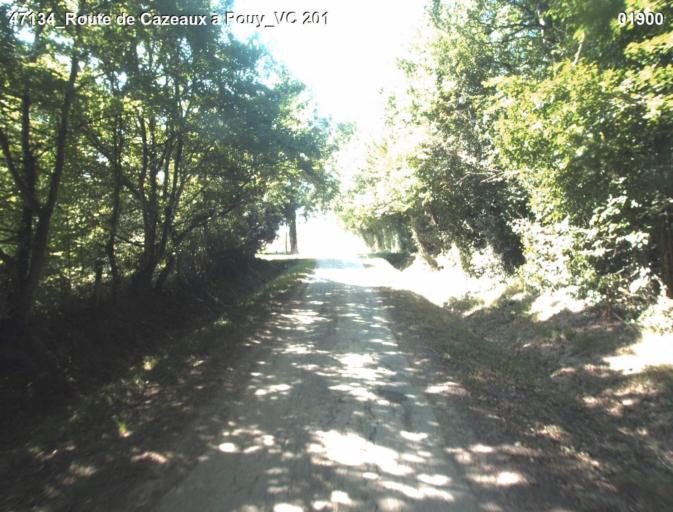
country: FR
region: Aquitaine
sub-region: Departement du Lot-et-Garonne
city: Mezin
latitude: 44.0181
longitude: 0.3119
